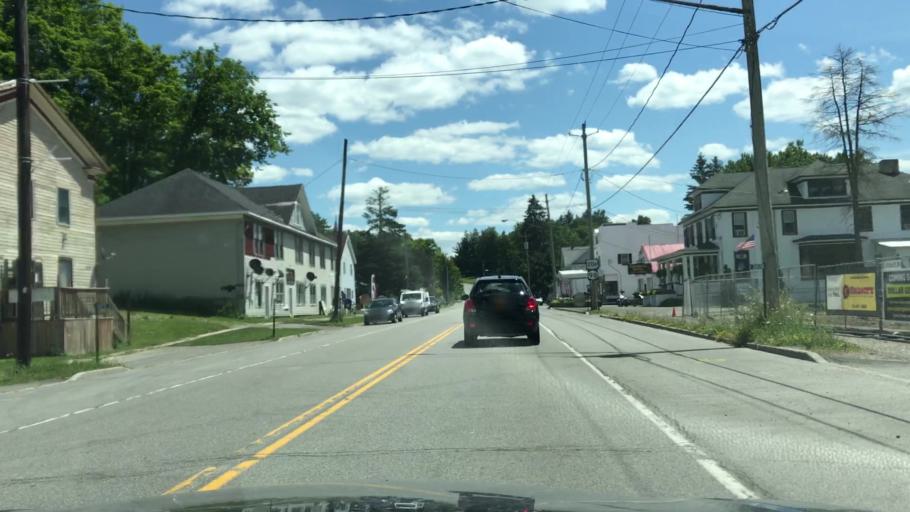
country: US
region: New York
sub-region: Wyoming County
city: Attica
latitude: 42.7617
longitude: -78.3130
